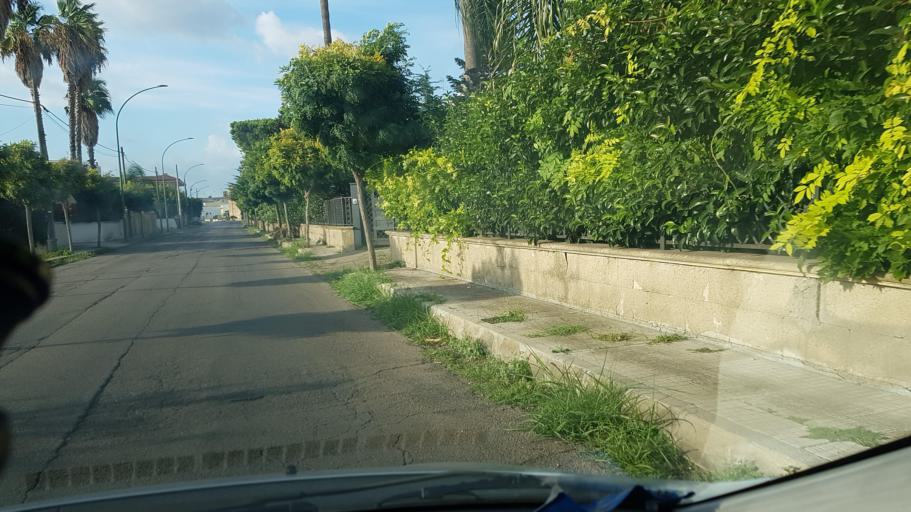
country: IT
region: Apulia
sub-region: Provincia di Lecce
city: Veglie
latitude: 40.3287
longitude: 17.9743
